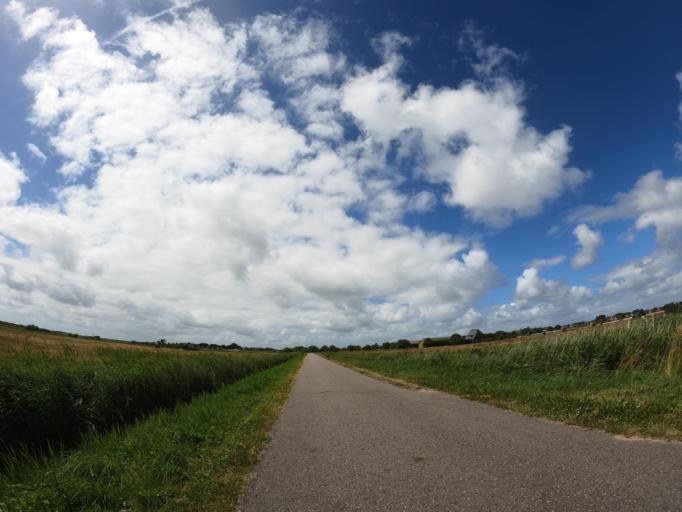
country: DE
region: Schleswig-Holstein
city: Tinnum
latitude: 54.8911
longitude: 8.3386
